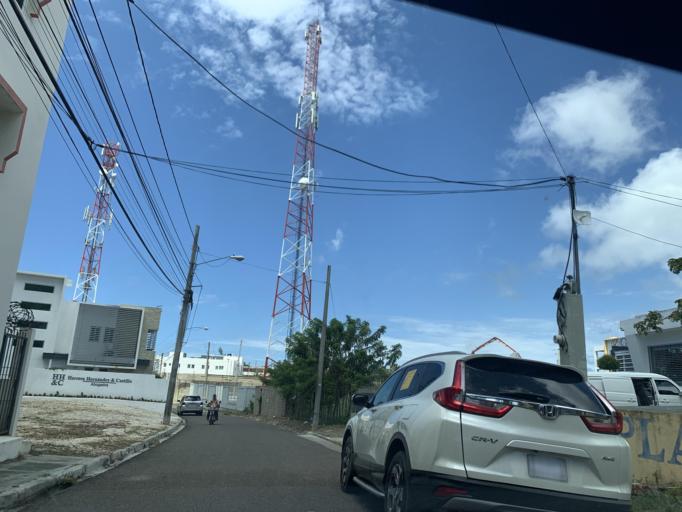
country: DO
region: Puerto Plata
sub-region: Puerto Plata
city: Puerto Plata
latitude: 19.7852
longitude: -70.6736
